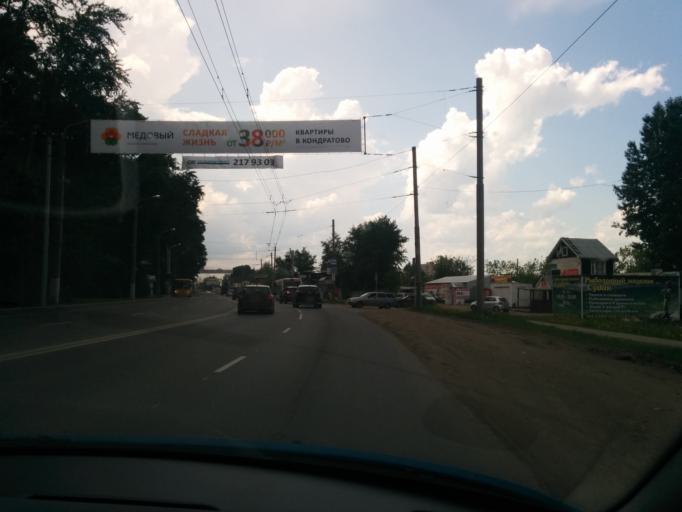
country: RU
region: Perm
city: Kondratovo
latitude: 57.9735
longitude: 56.1576
